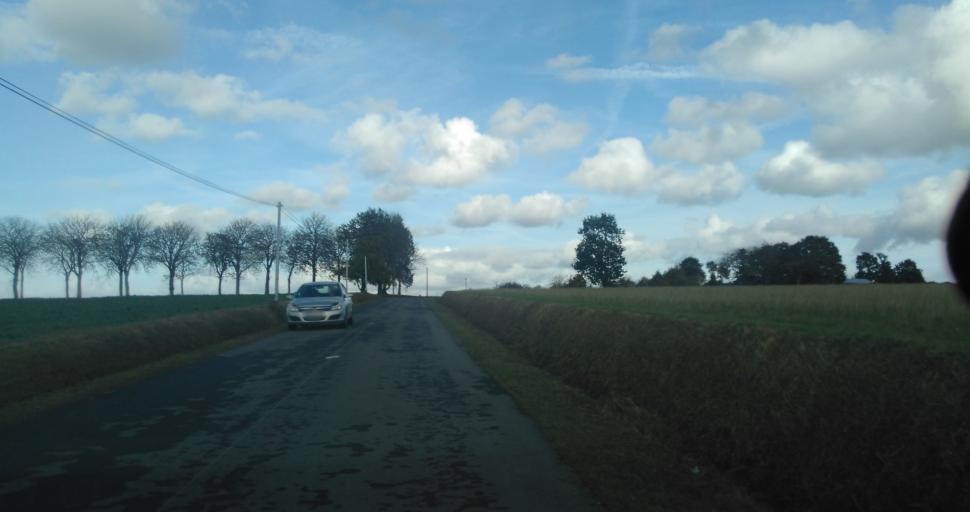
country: FR
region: Brittany
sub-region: Departement d'Ille-et-Vilaine
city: Boisgervilly
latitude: 48.1417
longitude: -2.0803
